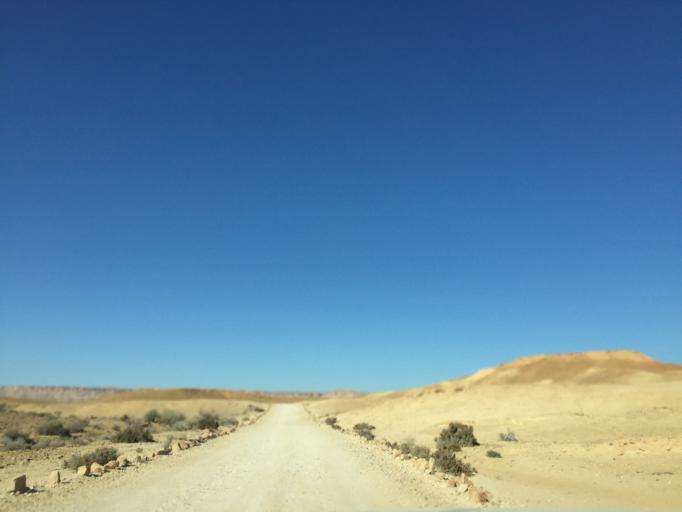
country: IL
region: Southern District
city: Mitzpe Ramon
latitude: 30.6163
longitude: 34.9313
